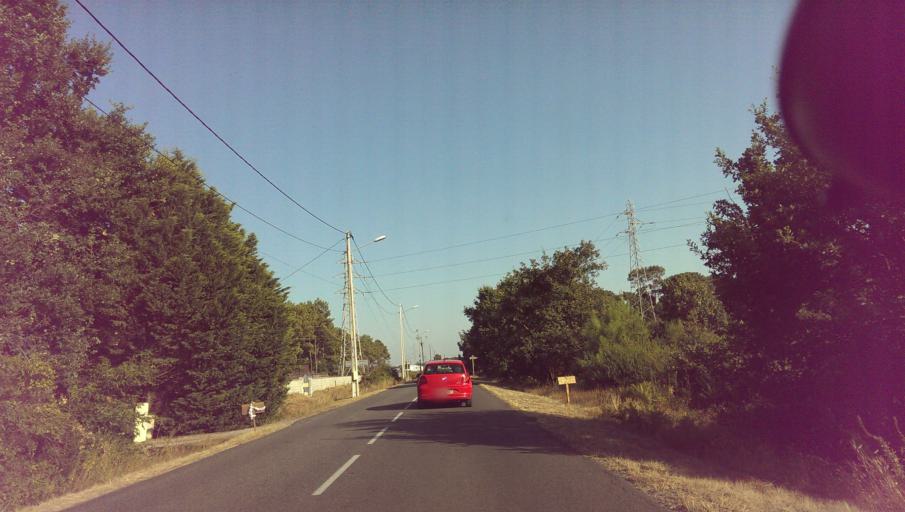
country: FR
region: Aquitaine
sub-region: Departement des Landes
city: Mimizan
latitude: 44.1943
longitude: -1.2204
